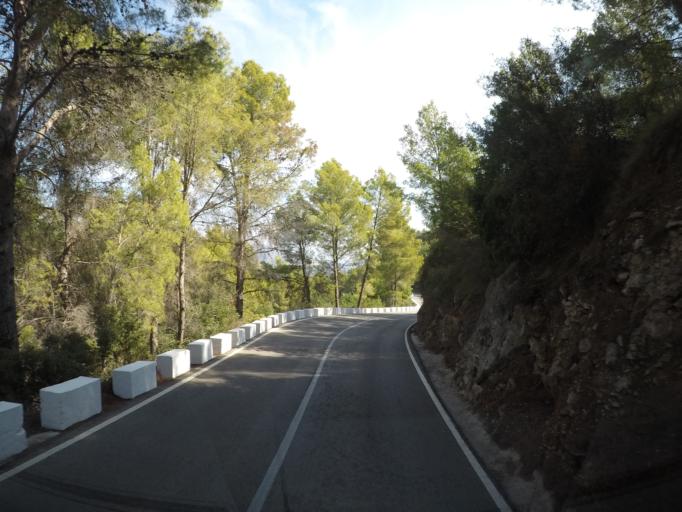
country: ES
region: Valencia
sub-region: Provincia de Alicante
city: Murla
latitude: 38.7833
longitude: -0.0889
